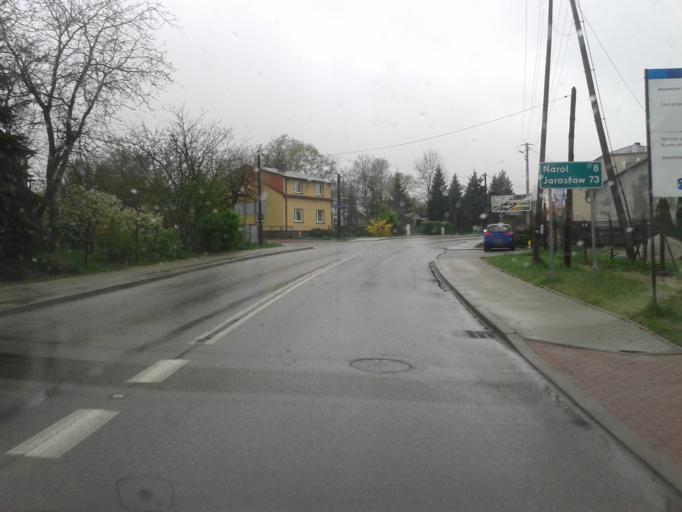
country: PL
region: Lublin Voivodeship
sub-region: Powiat tomaszowski
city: Belzec
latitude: 50.3843
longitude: 23.4375
